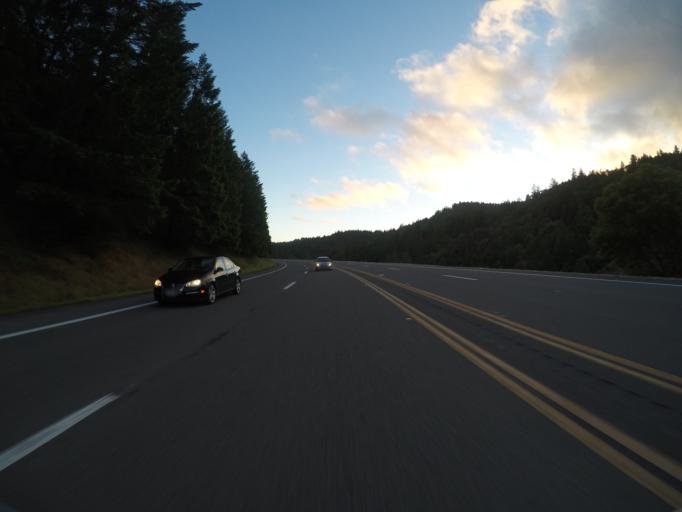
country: US
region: California
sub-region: Humboldt County
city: Redway
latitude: 39.9889
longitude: -123.7929
